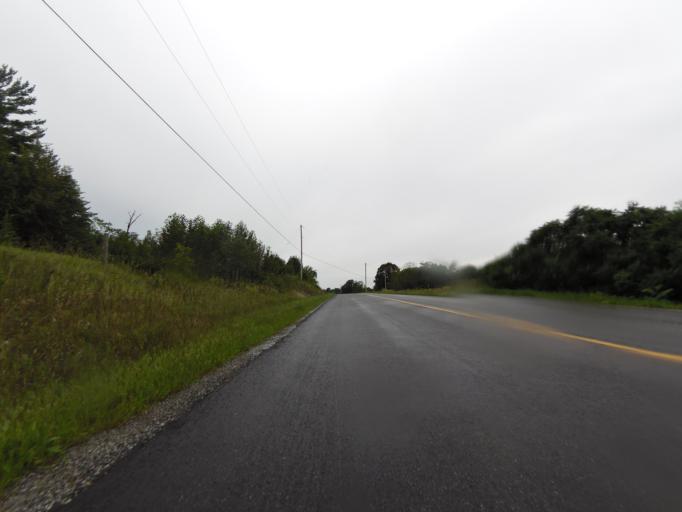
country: CA
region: Ontario
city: Perth
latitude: 44.9231
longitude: -76.4639
